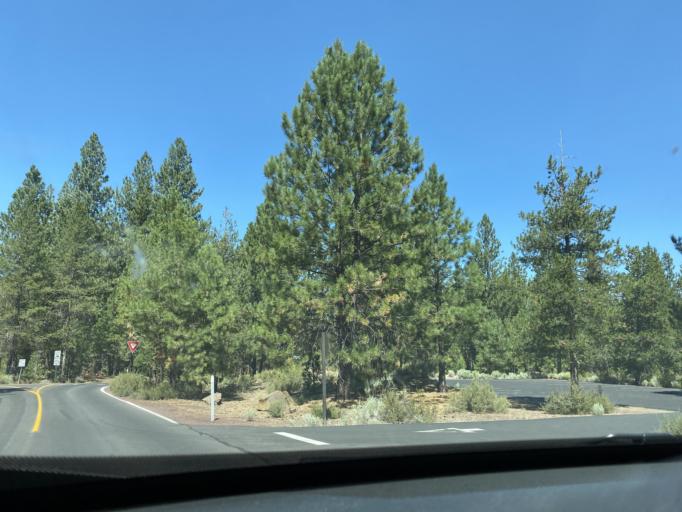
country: US
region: Oregon
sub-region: Deschutes County
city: Sunriver
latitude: 43.8785
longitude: -121.4337
